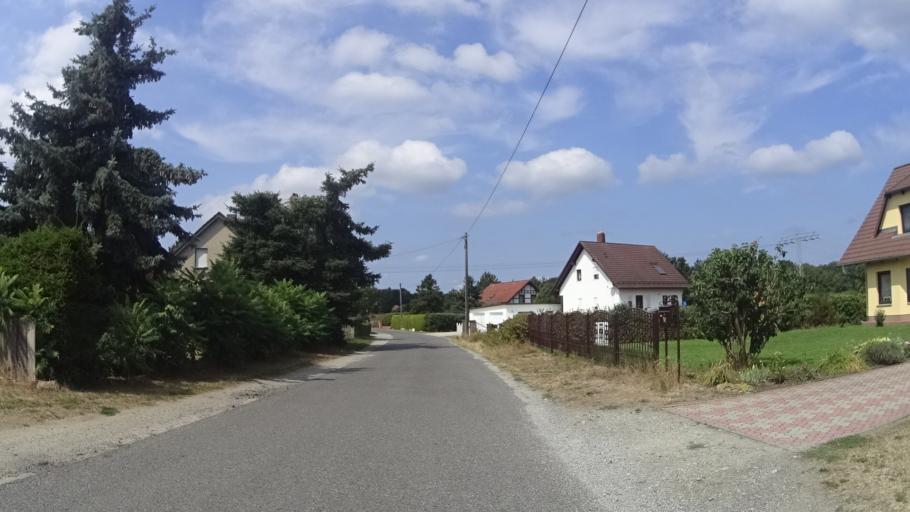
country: DE
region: Brandenburg
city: Tschernitz
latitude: 51.5823
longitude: 14.6115
